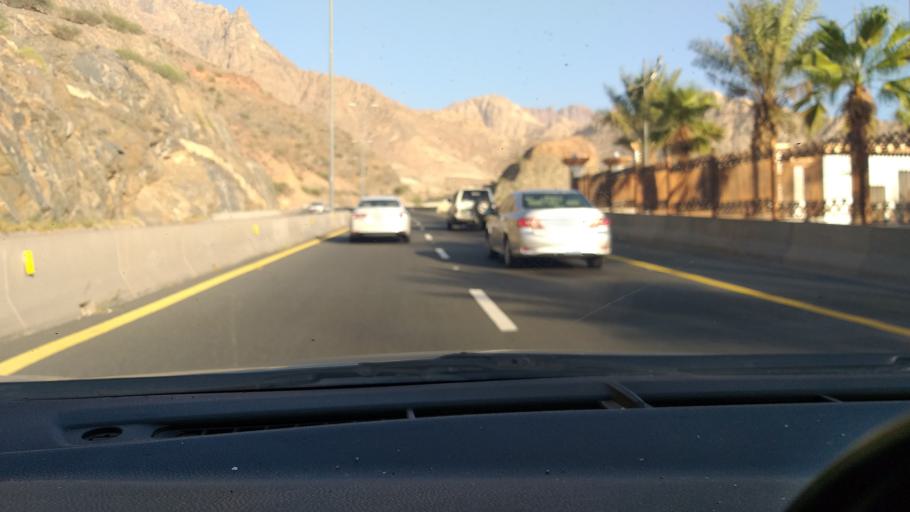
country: SA
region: Makkah
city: Al Hada
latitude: 21.3492
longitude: 40.2446
